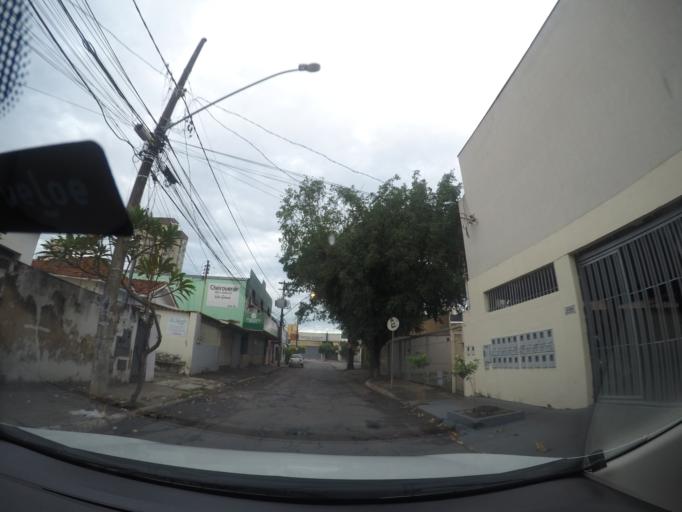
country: BR
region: Goias
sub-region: Goiania
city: Goiania
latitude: -16.6671
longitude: -49.2577
